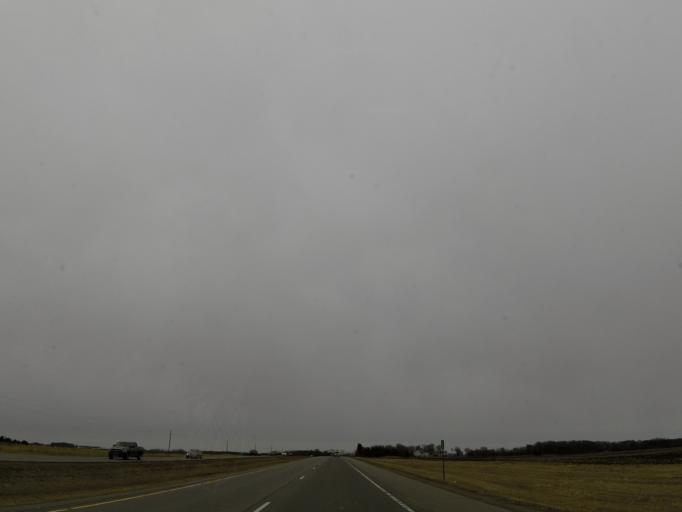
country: US
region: Minnesota
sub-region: Le Sueur County
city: Le Sueur
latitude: 44.5106
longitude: -93.8541
